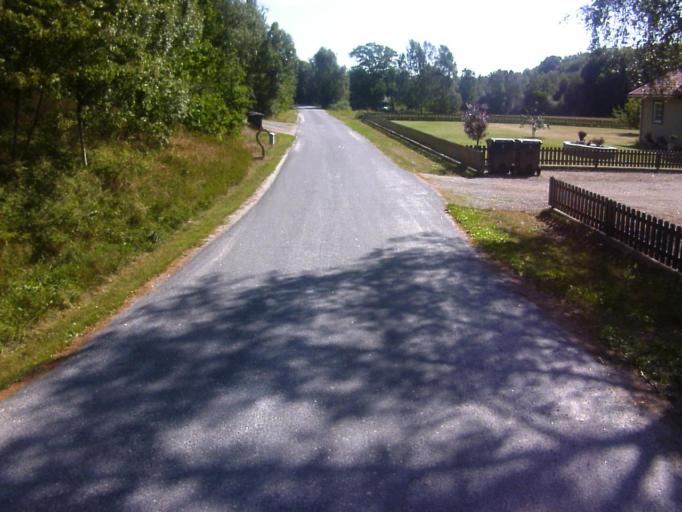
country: SE
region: Blekinge
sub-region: Solvesborgs Kommun
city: Soelvesborg
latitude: 56.1033
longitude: 14.6116
